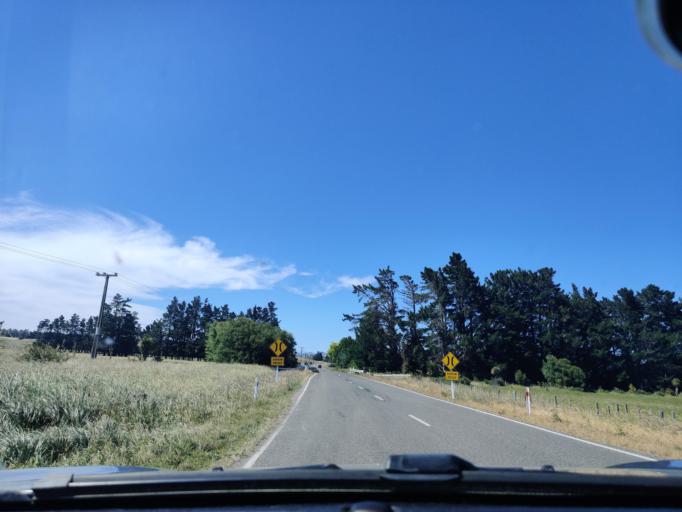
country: NZ
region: Wellington
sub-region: South Wairarapa District
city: Waipawa
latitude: -41.1914
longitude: 175.3596
